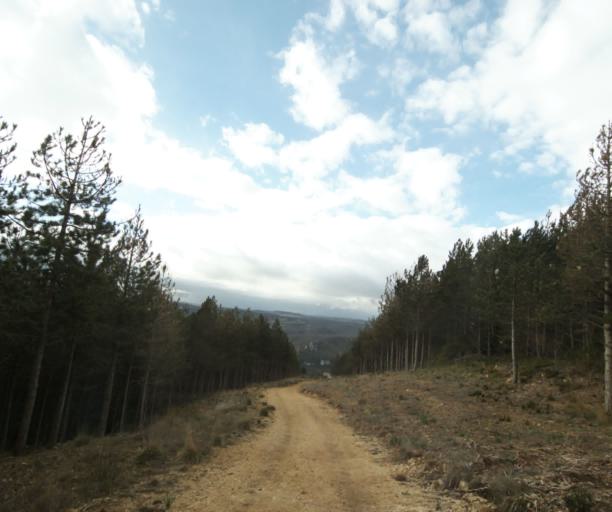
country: FR
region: Midi-Pyrenees
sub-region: Departement de l'Aveyron
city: Millau
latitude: 44.1170
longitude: 3.1516
